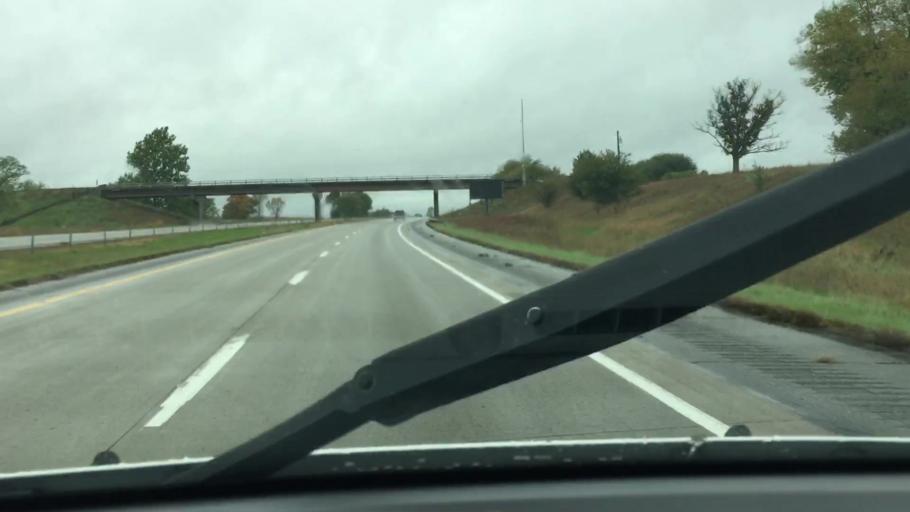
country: US
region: Iowa
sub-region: Jasper County
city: Newton
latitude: 41.6801
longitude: -92.9400
